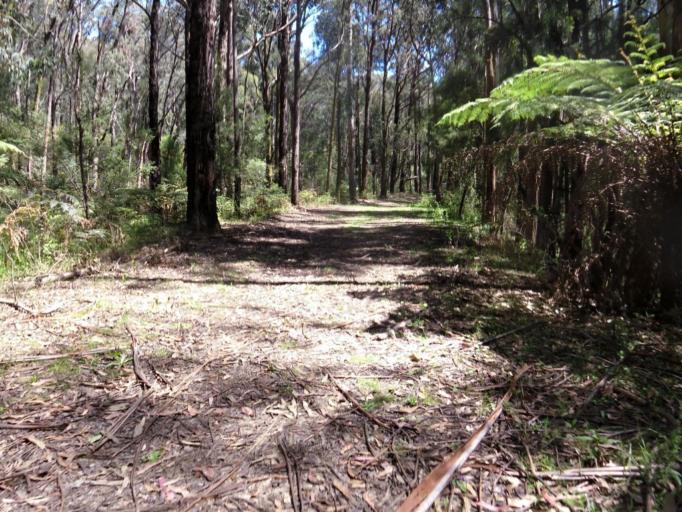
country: AU
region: Victoria
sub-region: Baw Baw
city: Warragul
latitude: -37.9031
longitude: 145.9795
